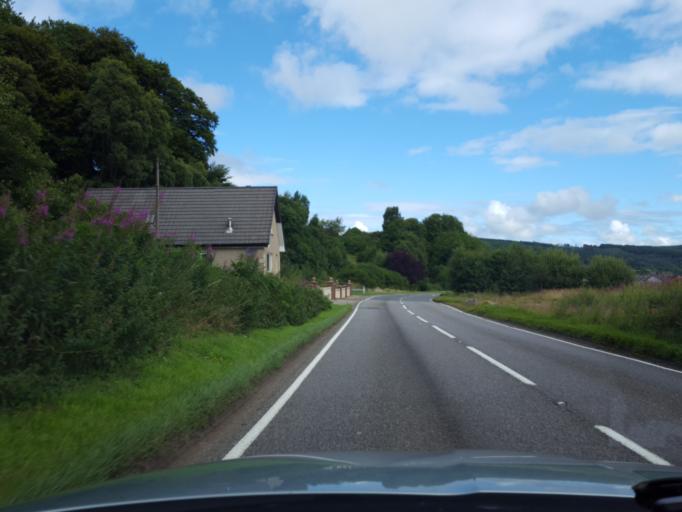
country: GB
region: Scotland
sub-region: Moray
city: Rothes
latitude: 57.5191
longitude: -3.2093
